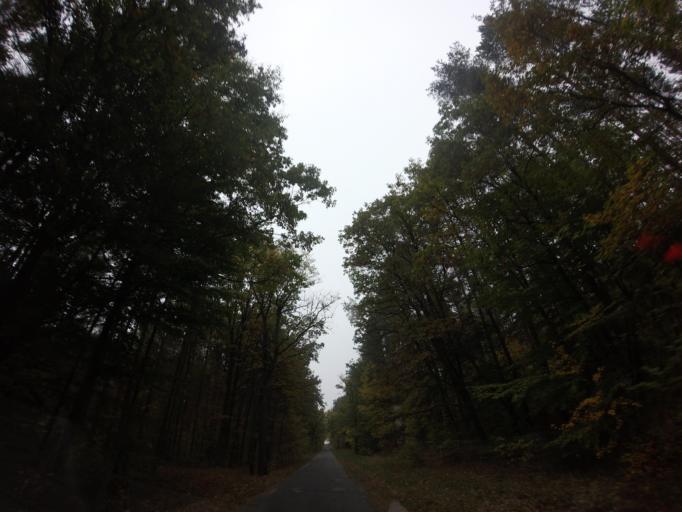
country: PL
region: West Pomeranian Voivodeship
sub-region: Powiat choszczenski
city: Krzecin
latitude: 53.0287
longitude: 15.5337
